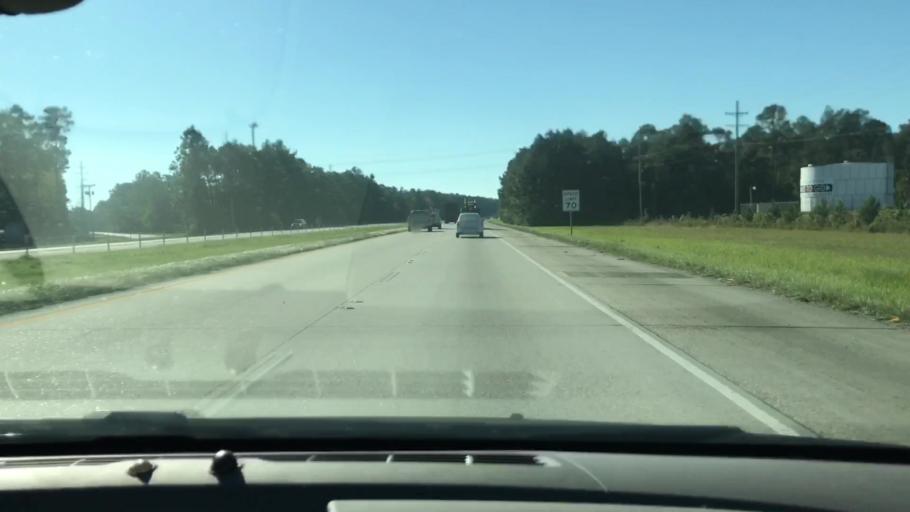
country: US
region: Louisiana
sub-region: Saint Tammany Parish
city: Pearl River
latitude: 30.3450
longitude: -89.7392
